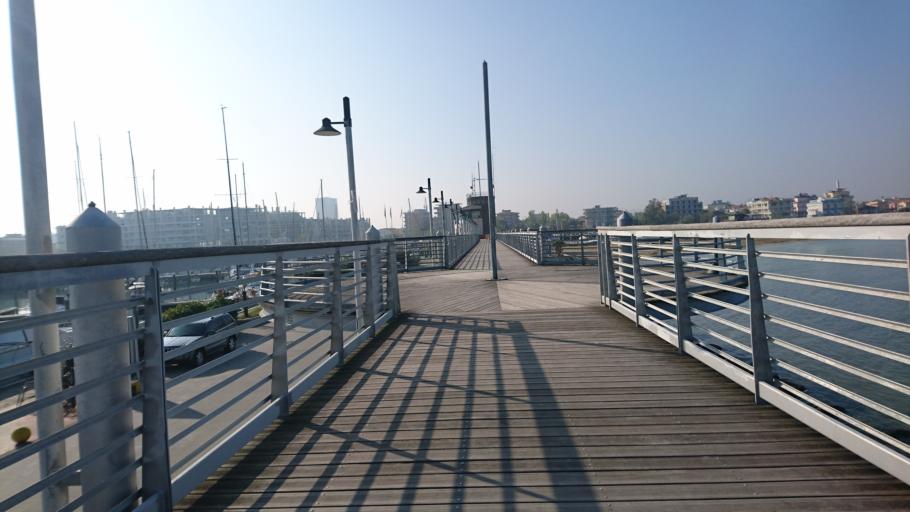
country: IT
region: Emilia-Romagna
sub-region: Provincia di Rimini
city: Rimini
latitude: 44.0774
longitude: 12.5702
